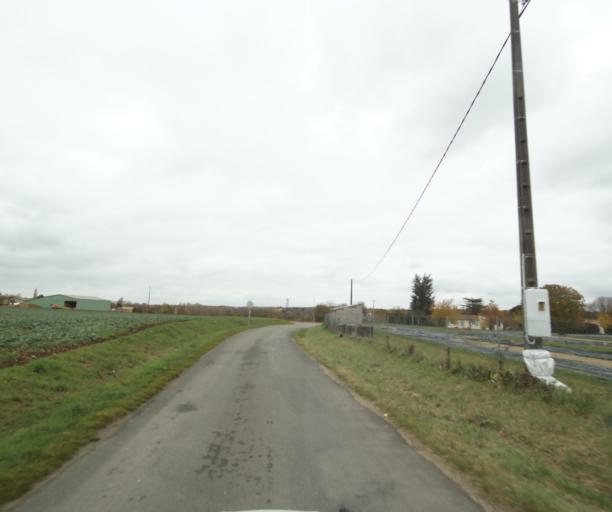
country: FR
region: Poitou-Charentes
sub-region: Departement de la Charente-Maritime
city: Bussac-sur-Charente
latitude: 45.7740
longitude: -0.6424
